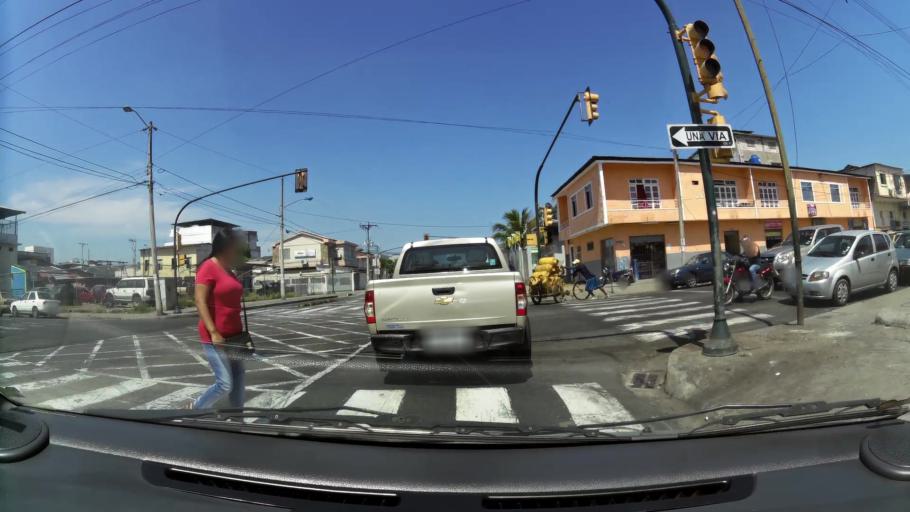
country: EC
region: Guayas
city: Guayaquil
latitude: -2.1925
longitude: -79.8962
